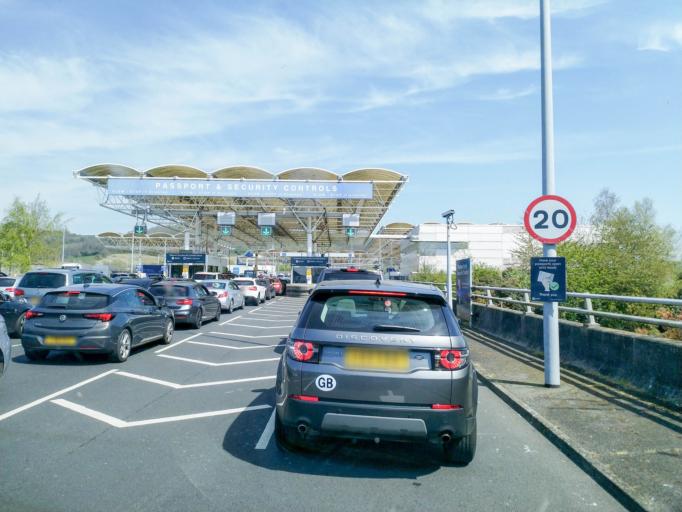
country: GB
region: England
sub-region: Kent
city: Hythe
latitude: 51.0938
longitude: 1.1219
